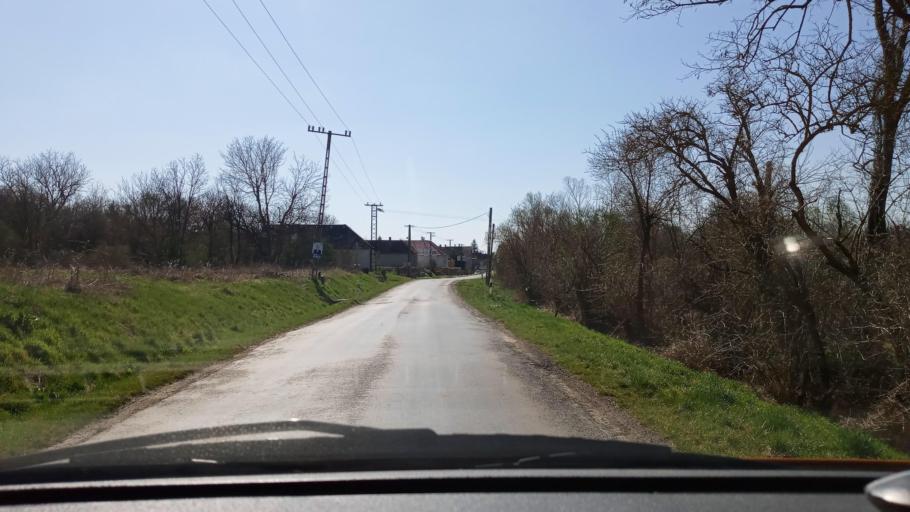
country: HU
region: Baranya
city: Kozarmisleny
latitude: 46.0637
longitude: 18.3727
